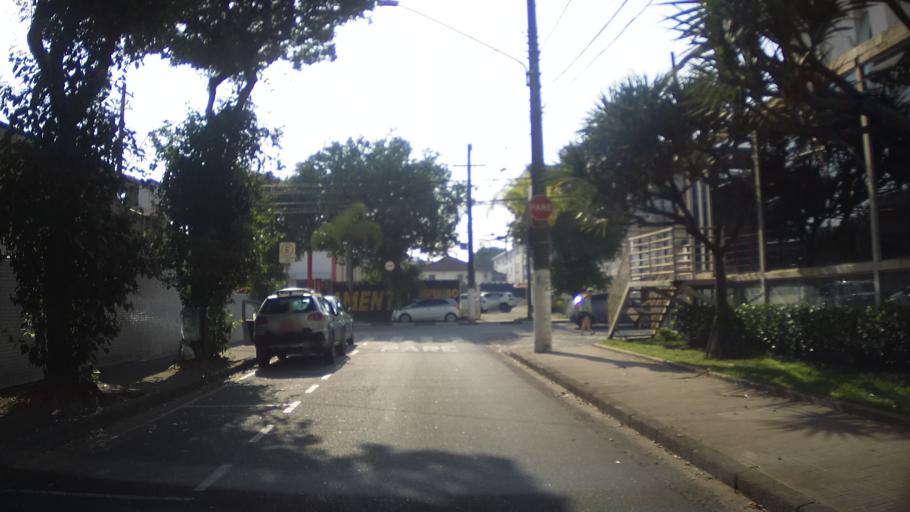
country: BR
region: Sao Paulo
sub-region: Santos
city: Santos
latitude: -23.9621
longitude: -46.3236
